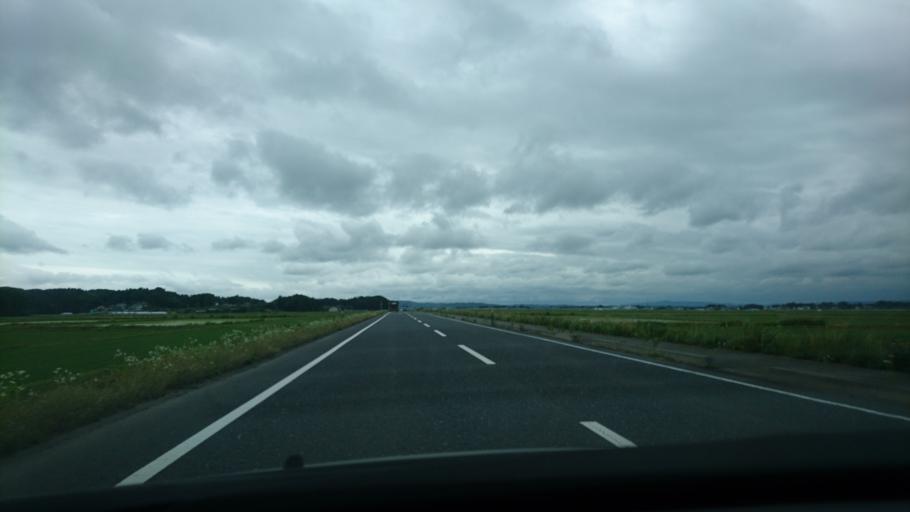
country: JP
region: Miyagi
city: Wakuya
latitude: 38.7050
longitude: 141.2601
